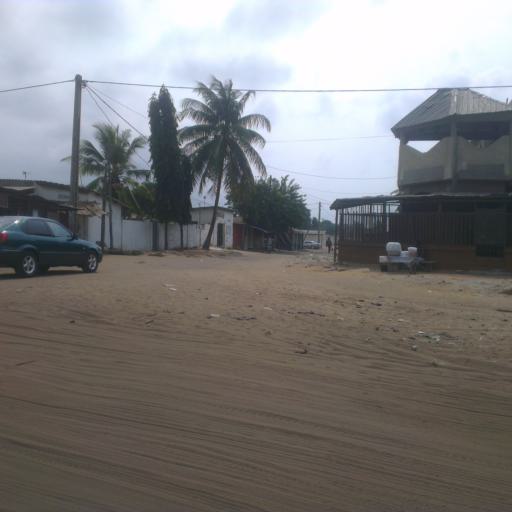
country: TG
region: Maritime
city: Lome
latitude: 6.1671
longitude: 1.3016
